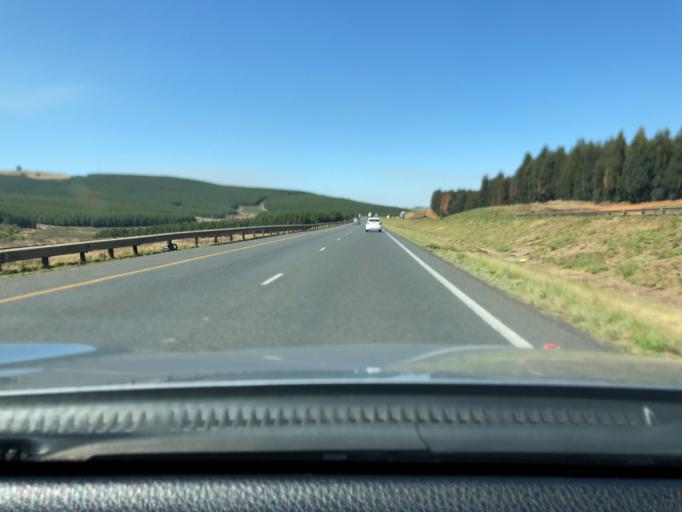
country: ZA
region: KwaZulu-Natal
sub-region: uMgungundlovu District Municipality
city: Howick
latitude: -29.3824
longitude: 30.1291
